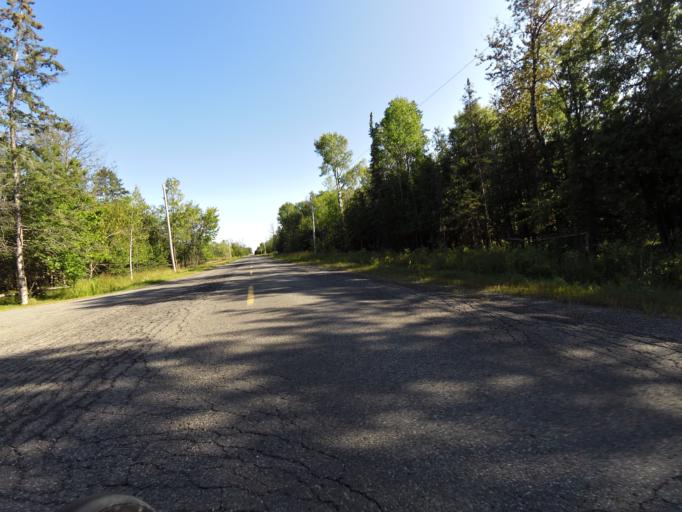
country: CA
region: Ontario
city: Bells Corners
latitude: 45.4705
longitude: -76.0123
